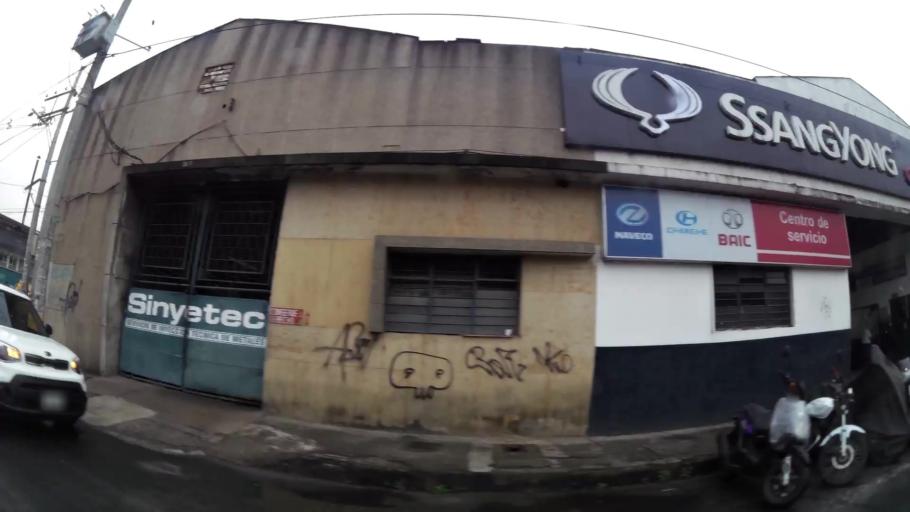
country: CO
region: Antioquia
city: Medellin
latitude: 6.2276
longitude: -75.5724
